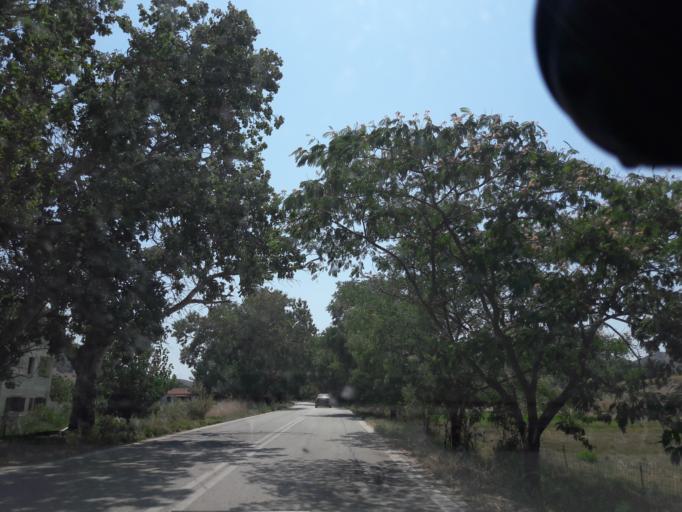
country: GR
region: North Aegean
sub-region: Nomos Lesvou
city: Myrina
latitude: 39.8698
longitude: 25.1565
